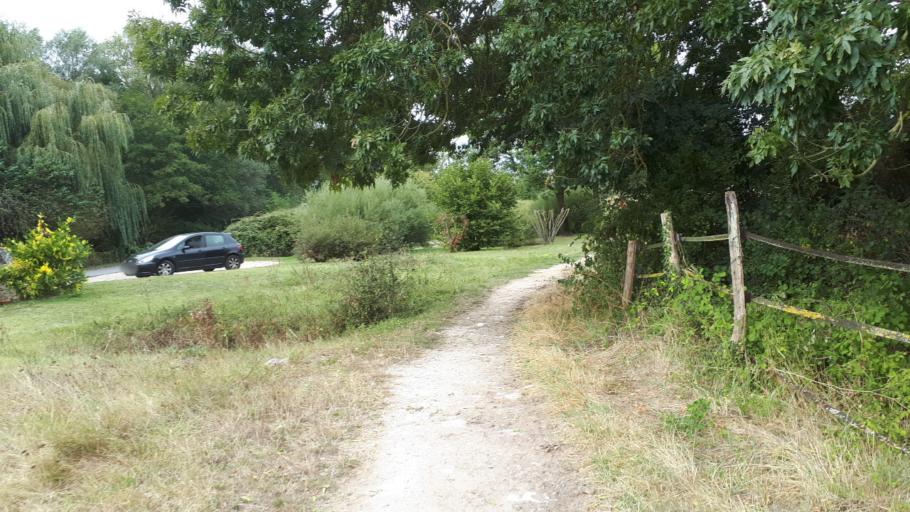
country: FR
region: Centre
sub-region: Departement du Loir-et-Cher
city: Saint-Gervais-la-Foret
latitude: 47.5673
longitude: 1.3459
